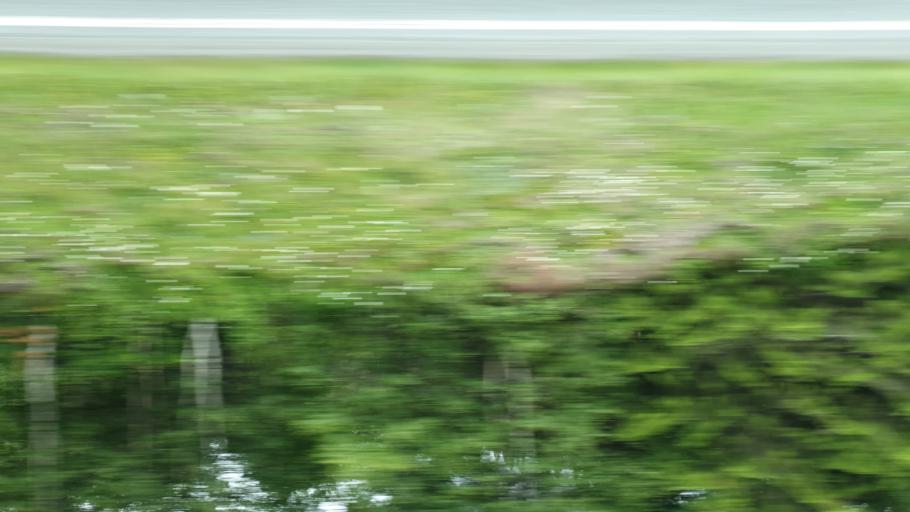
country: NO
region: Sor-Trondelag
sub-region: Rennebu
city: Berkak
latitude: 62.8684
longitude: 10.0289
